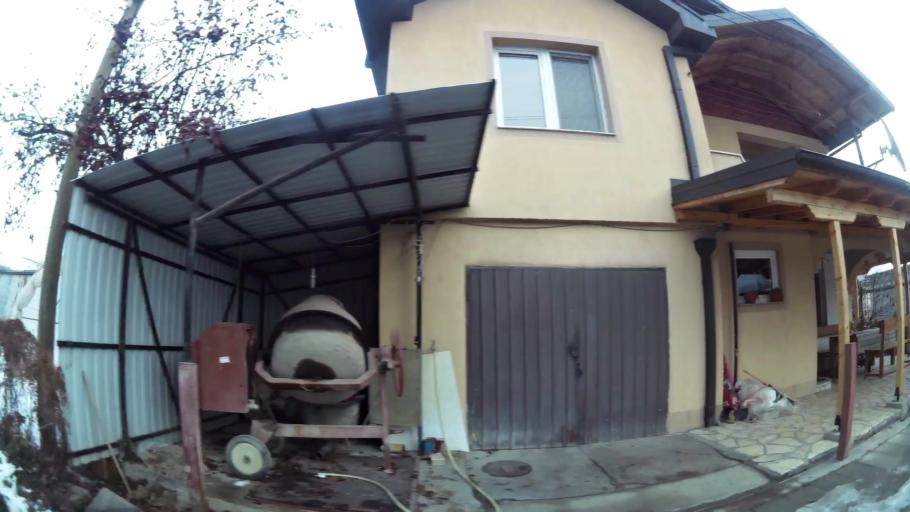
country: MK
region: Ilinden
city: Jurumleri
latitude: 41.9679
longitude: 21.5609
